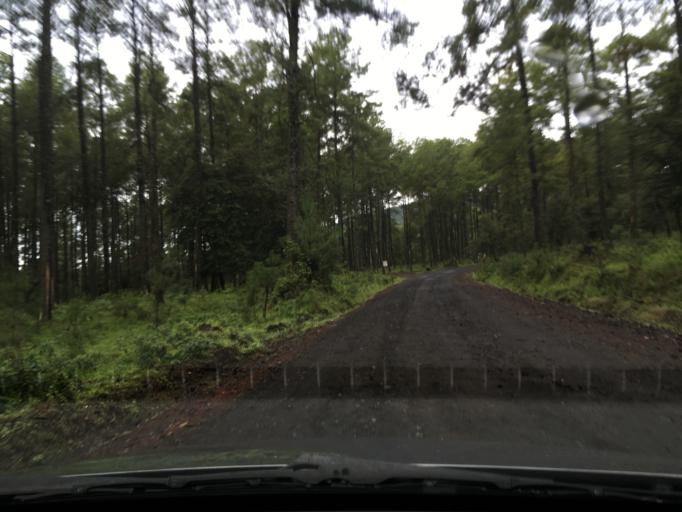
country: MX
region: Michoacan
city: Nuevo San Juan Parangaricutiro
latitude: 19.4439
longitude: -102.1804
